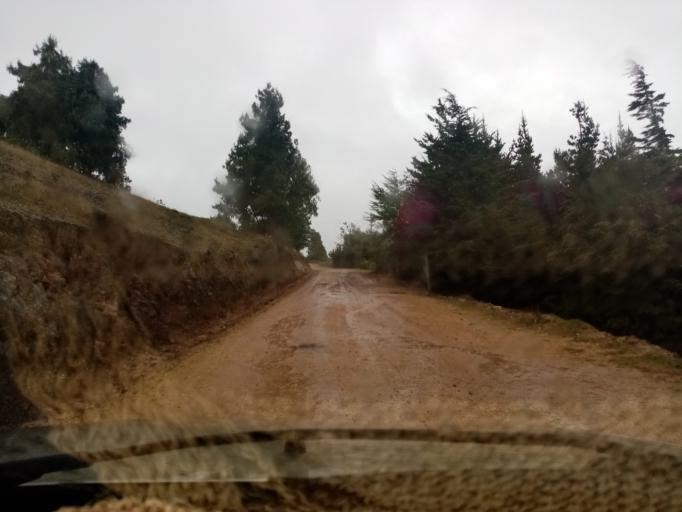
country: CO
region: Boyaca
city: Siachoque
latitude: 5.5549
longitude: -73.2808
